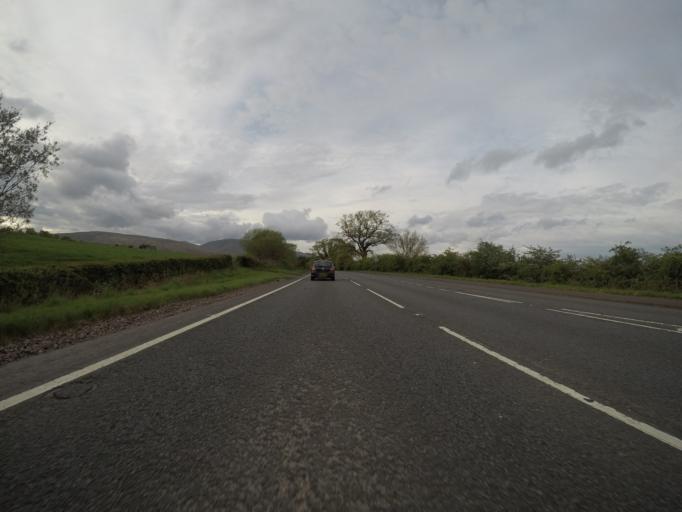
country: GB
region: Scotland
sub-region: West Dunbartonshire
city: Balloch
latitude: 56.0295
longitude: -4.6347
